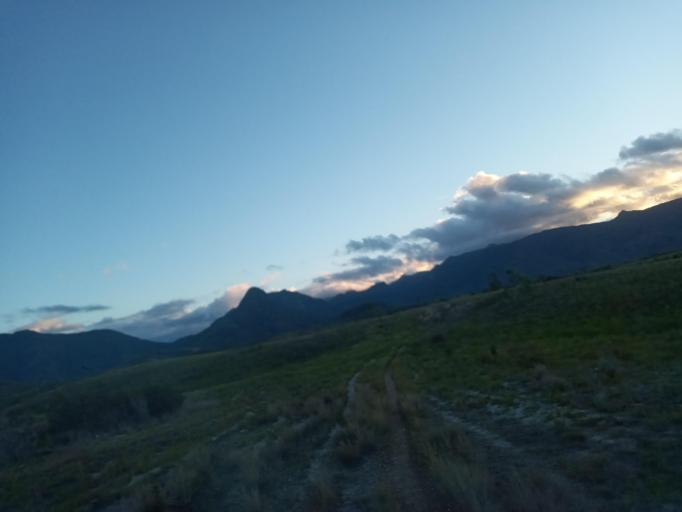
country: MG
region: Anosy
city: Fort Dauphin
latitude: -24.5131
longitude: 47.2355
